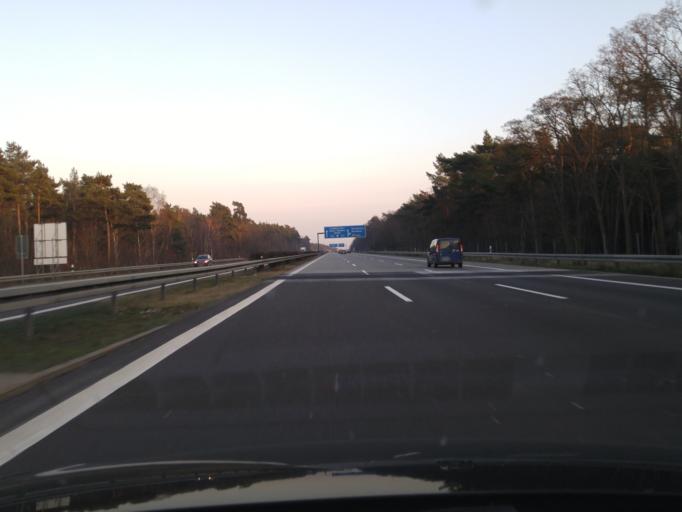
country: DE
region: Brandenburg
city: Brandenburg an der Havel
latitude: 52.3509
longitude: 12.5816
